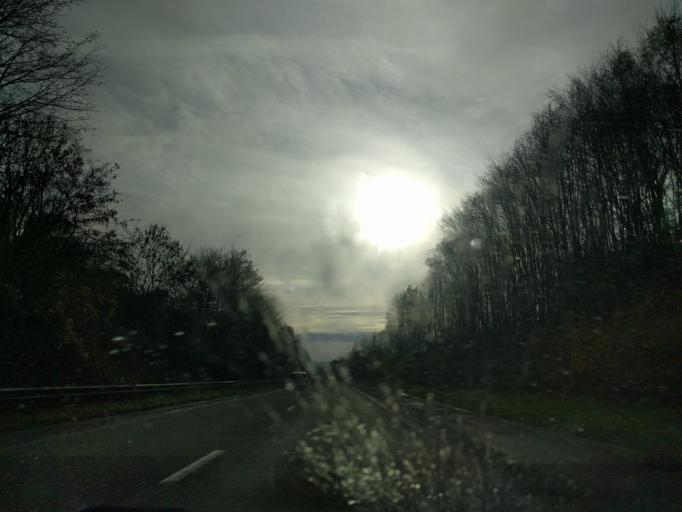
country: BE
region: Wallonia
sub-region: Province de Namur
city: Ciney
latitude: 50.2837
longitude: 5.0197
